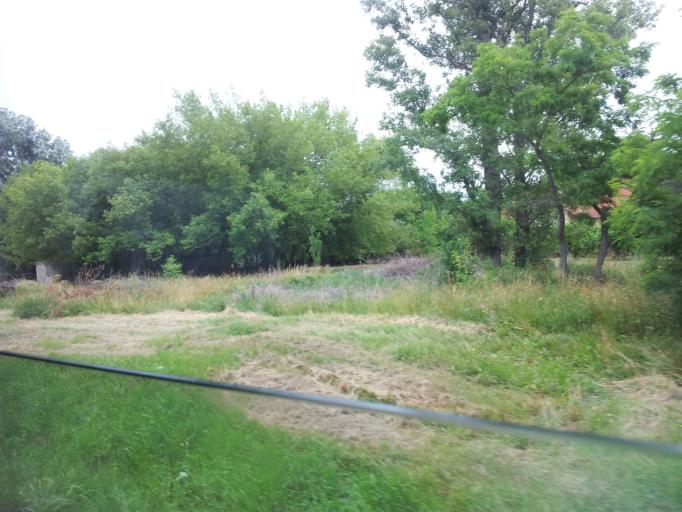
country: HU
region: Veszprem
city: Badacsonytomaj
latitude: 46.8069
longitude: 17.4683
